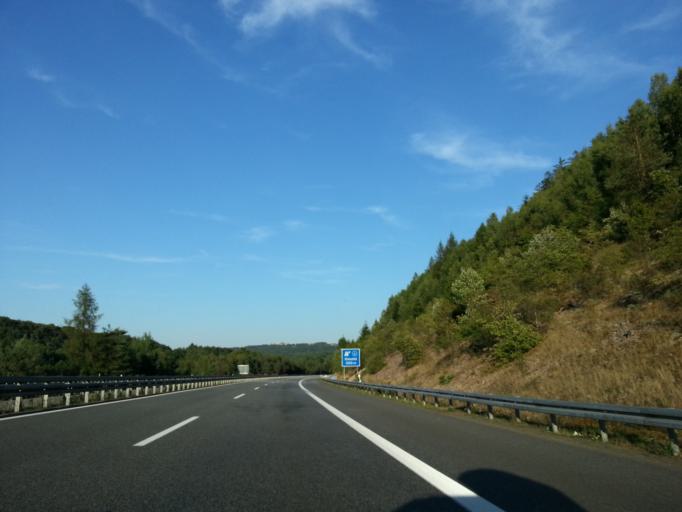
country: DE
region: Rheinland-Pfalz
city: Ellweiler
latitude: 49.6020
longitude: 7.1509
